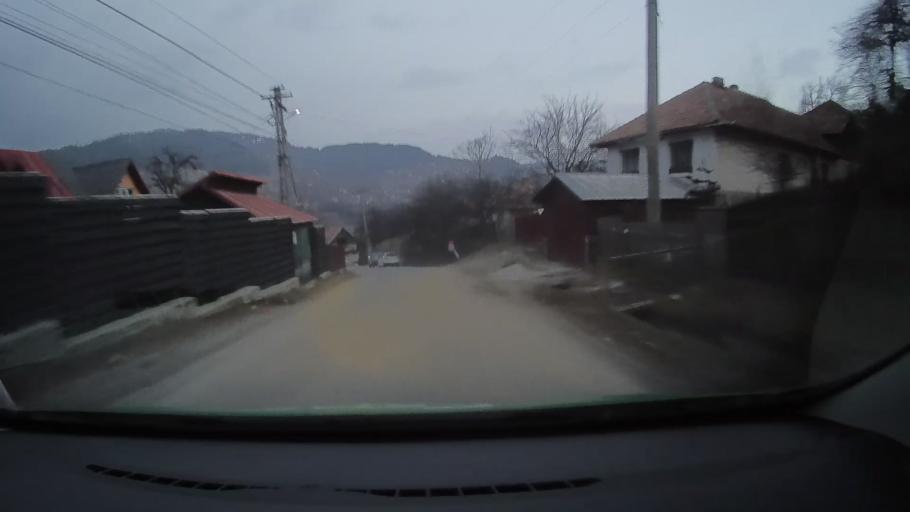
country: RO
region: Prahova
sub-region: Comuna Valea Doftanei
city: Tesila
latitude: 45.2975
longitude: 25.7184
